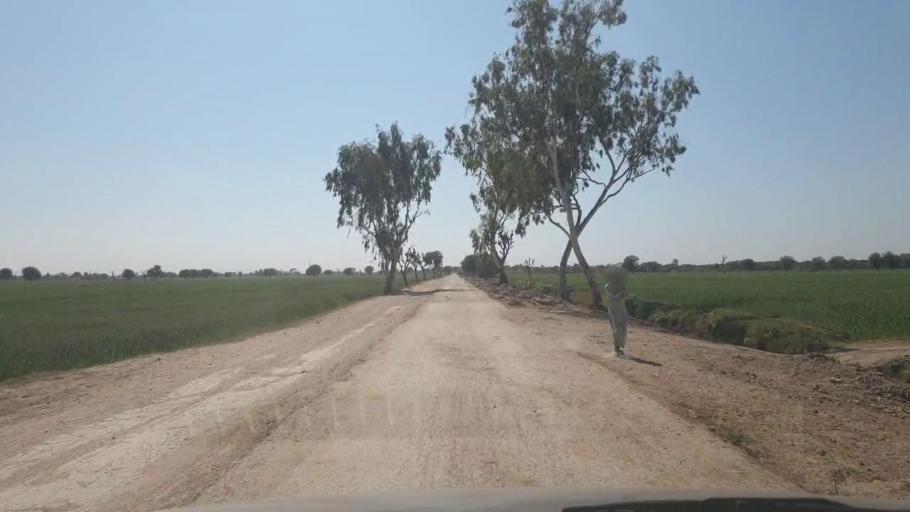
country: PK
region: Sindh
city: Dhoro Naro
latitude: 25.4763
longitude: 69.6103
